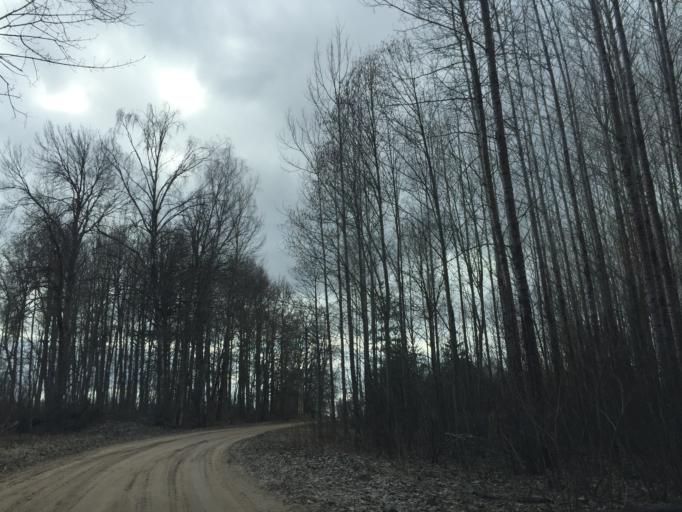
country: LV
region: Vecumnieki
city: Vecumnieki
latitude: 56.5791
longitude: 24.6075
